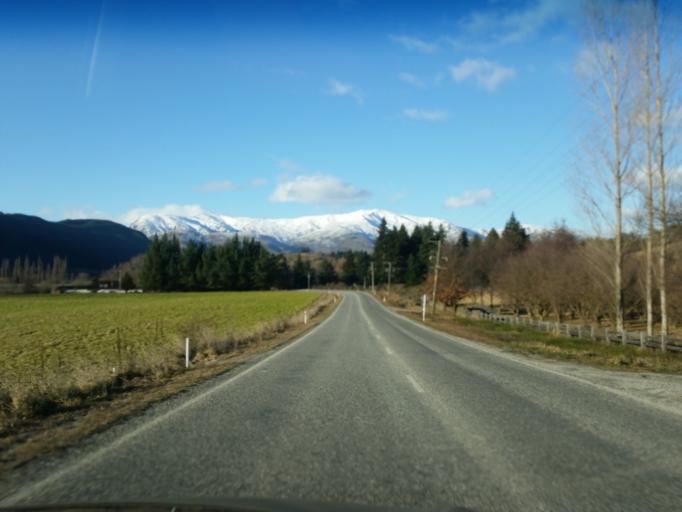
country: NZ
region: Otago
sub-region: Queenstown-Lakes District
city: Arrowtown
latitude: -44.9559
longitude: 168.7378
